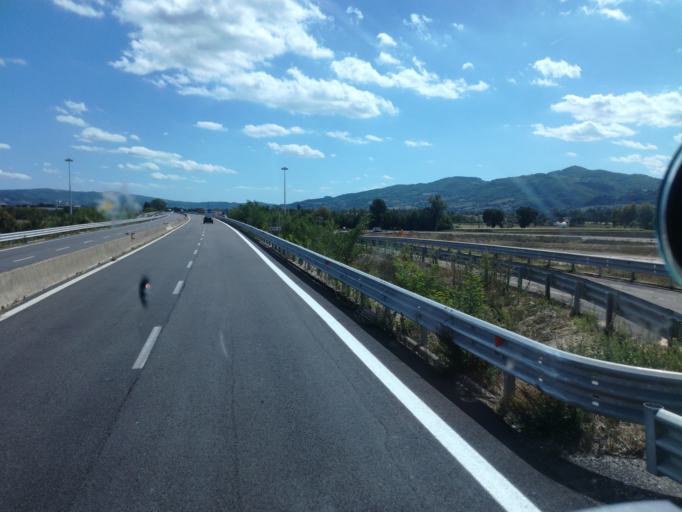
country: IT
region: Umbria
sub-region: Provincia di Perugia
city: Cerbara
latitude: 43.5023
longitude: 12.1941
